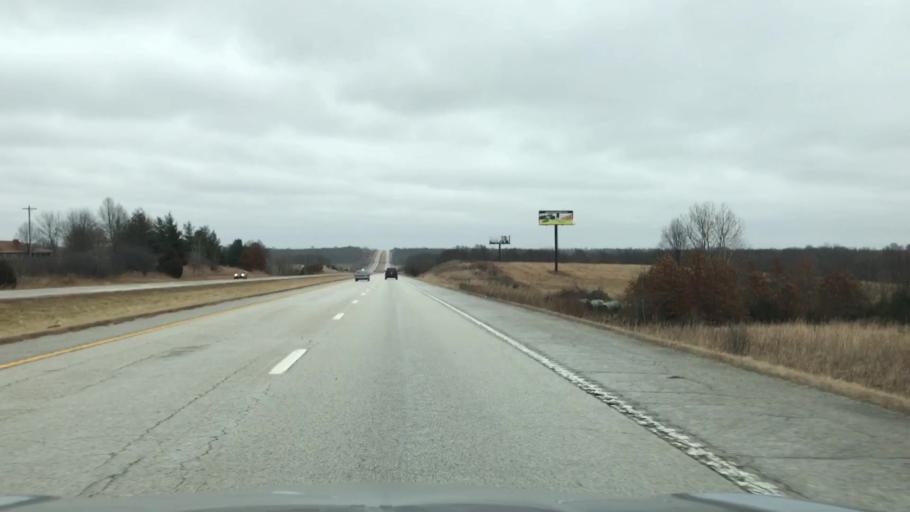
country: US
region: Missouri
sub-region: Clinton County
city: Cameron
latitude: 39.7520
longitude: -94.1840
